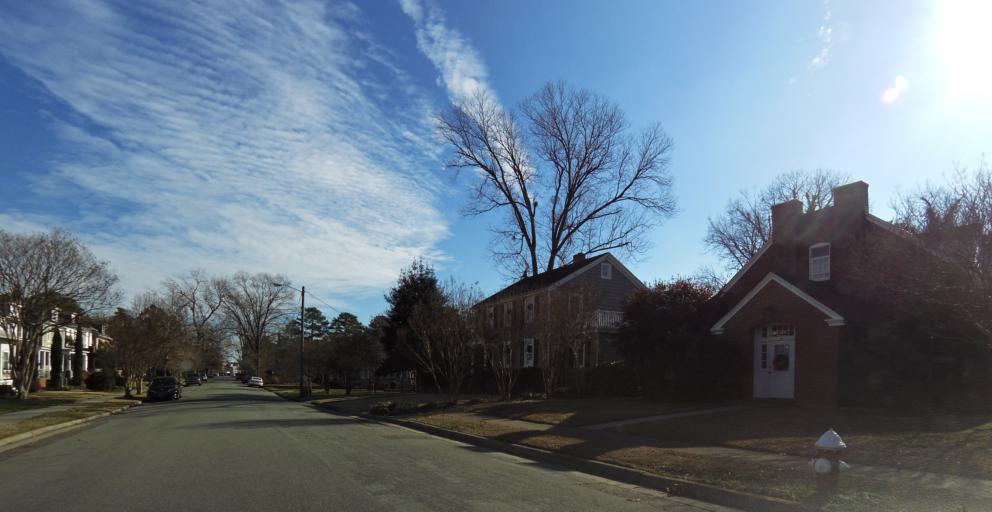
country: US
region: Virginia
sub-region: City of Hampton
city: Hampton
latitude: 37.0190
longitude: -76.3498
